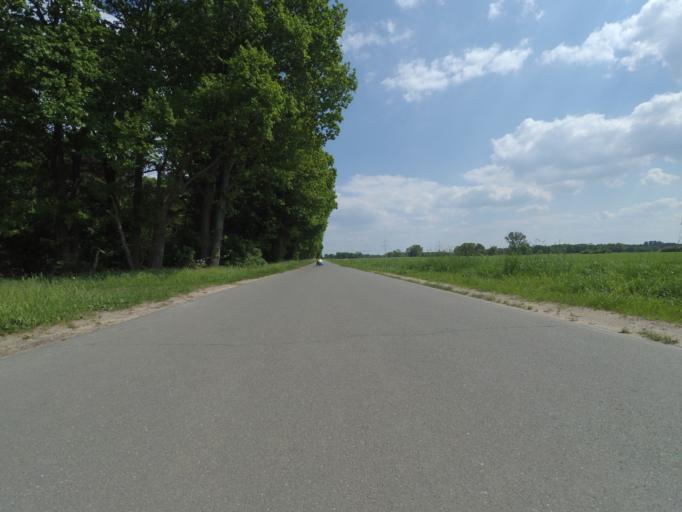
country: DE
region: Lower Saxony
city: Edemissen
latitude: 52.4551
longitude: 10.2781
